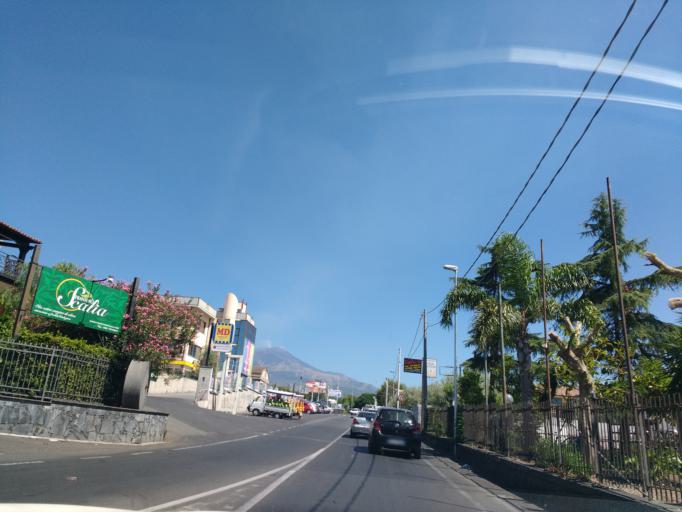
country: IT
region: Sicily
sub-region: Catania
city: Mascalucia
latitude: 37.5845
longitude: 15.0500
